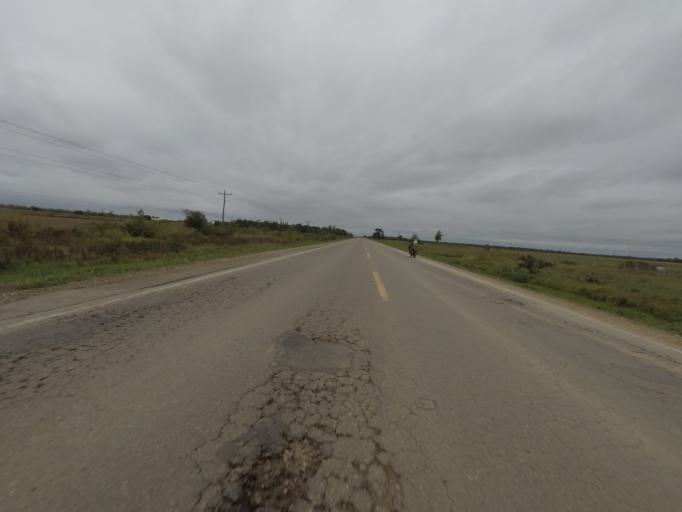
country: BO
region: Santa Cruz
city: Okinawa Numero Uno
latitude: -17.2919
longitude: -62.5553
